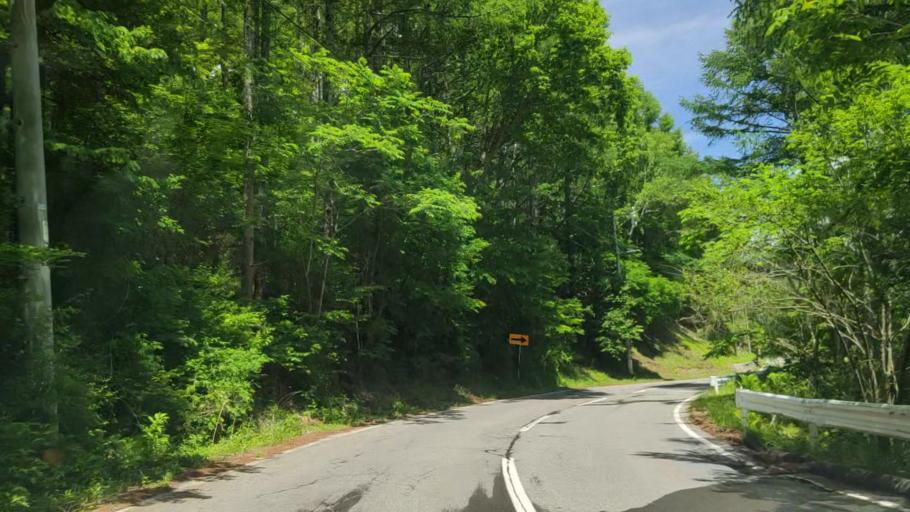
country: JP
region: Nagano
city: Suwa
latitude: 36.1189
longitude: 138.2295
